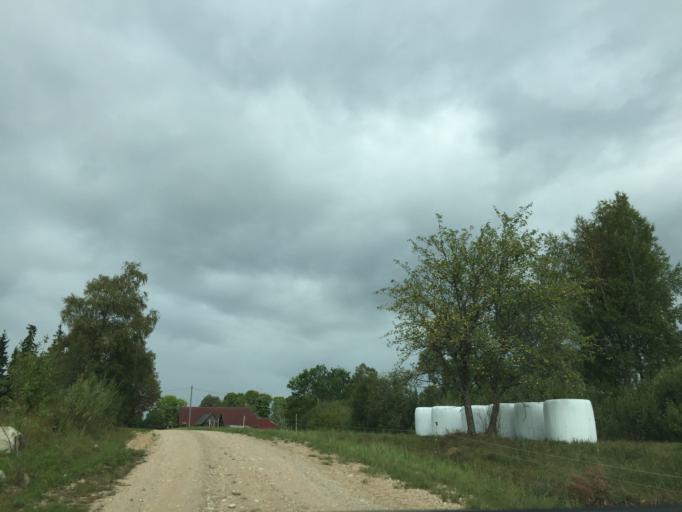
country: LV
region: Pargaujas
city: Stalbe
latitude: 57.5106
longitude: 24.9160
